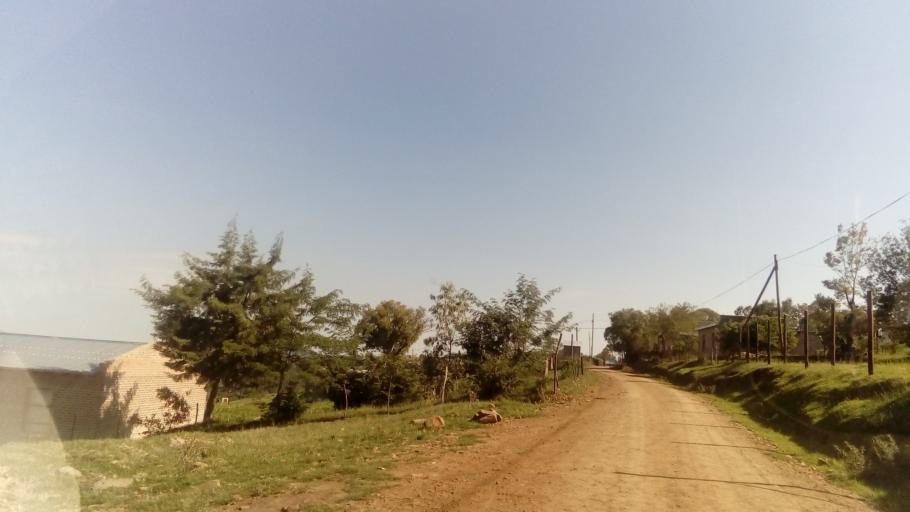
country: LS
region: Berea
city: Teyateyaneng
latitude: -29.1463
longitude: 27.7472
